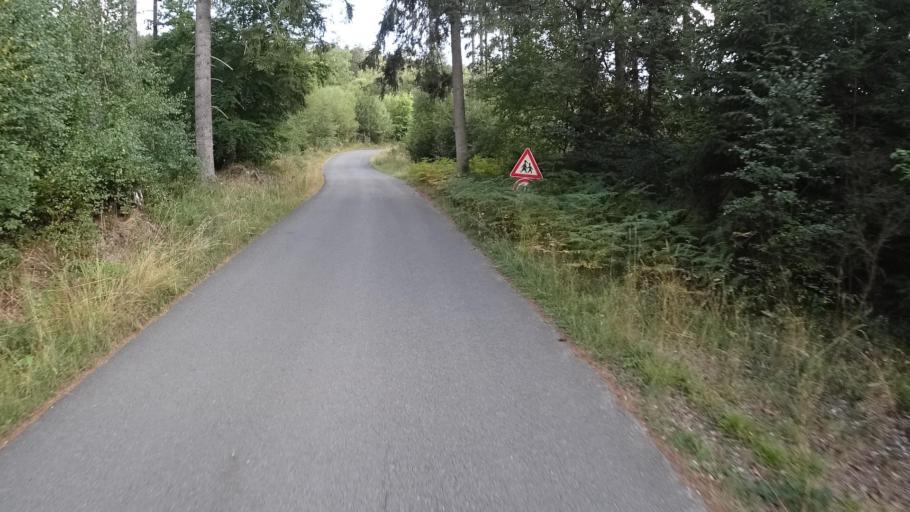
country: DE
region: Rheinland-Pfalz
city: Dichtelbach
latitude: 49.9916
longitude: 7.7069
